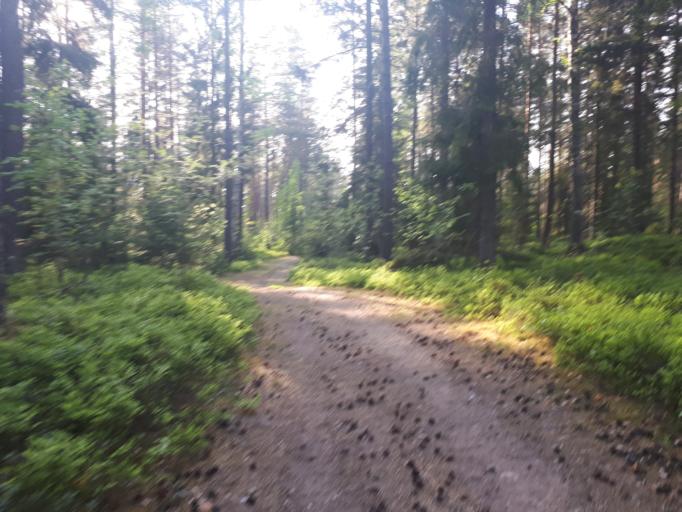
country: SE
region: Soedermanland
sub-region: Flens Kommun
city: Halleforsnas
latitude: 59.0646
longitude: 16.4004
